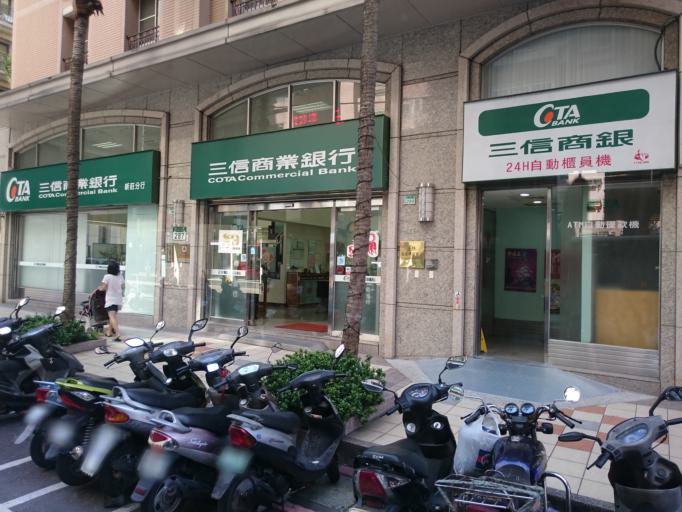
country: TW
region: Taipei
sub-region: Taipei
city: Banqiao
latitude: 25.0507
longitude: 121.4445
